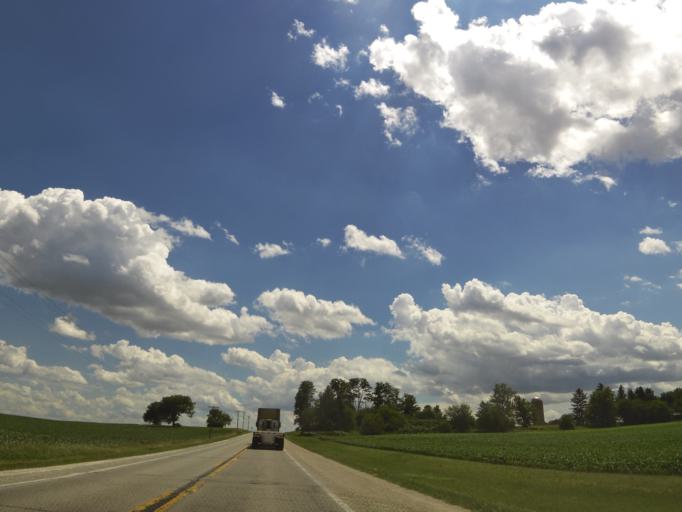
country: US
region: Iowa
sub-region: Benton County
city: Urbana
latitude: 42.3407
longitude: -91.8893
